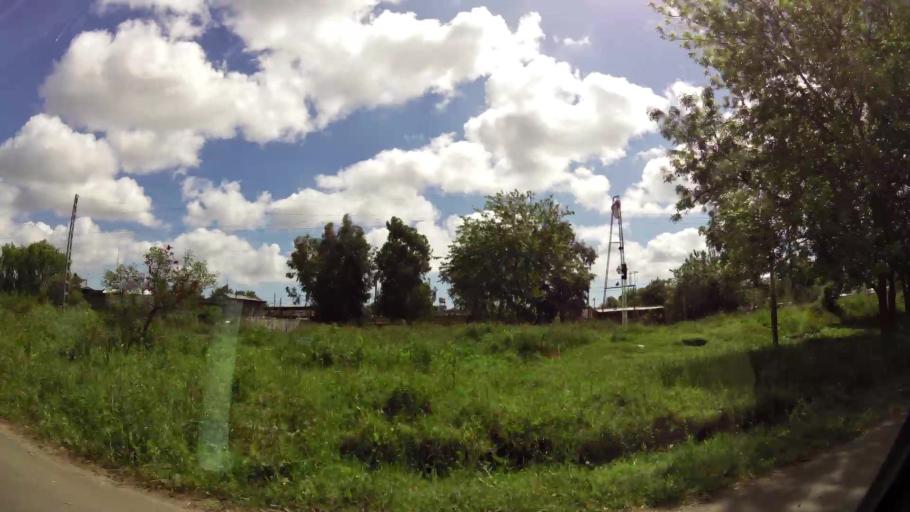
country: AR
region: Buenos Aires
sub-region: Partido de Quilmes
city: Quilmes
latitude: -34.8369
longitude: -58.1774
